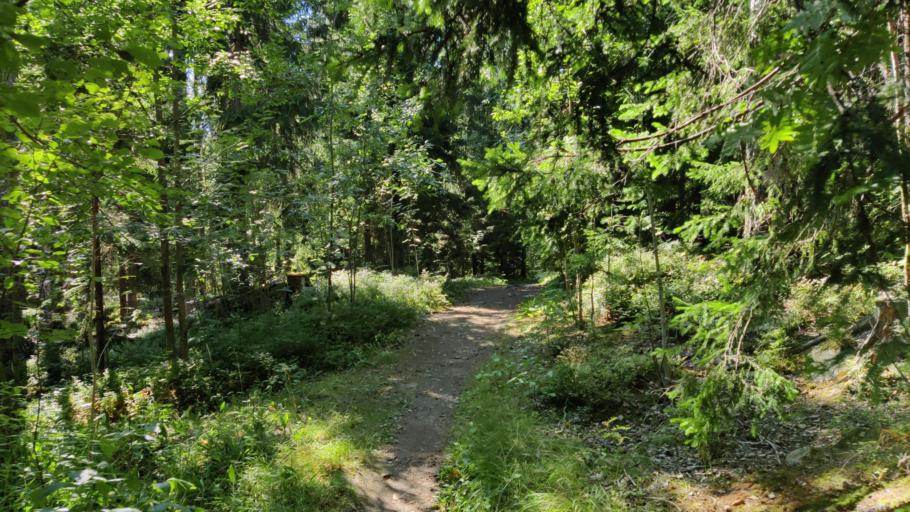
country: FI
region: Uusimaa
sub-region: Helsinki
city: Teekkarikylae
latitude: 60.2540
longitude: 24.8387
